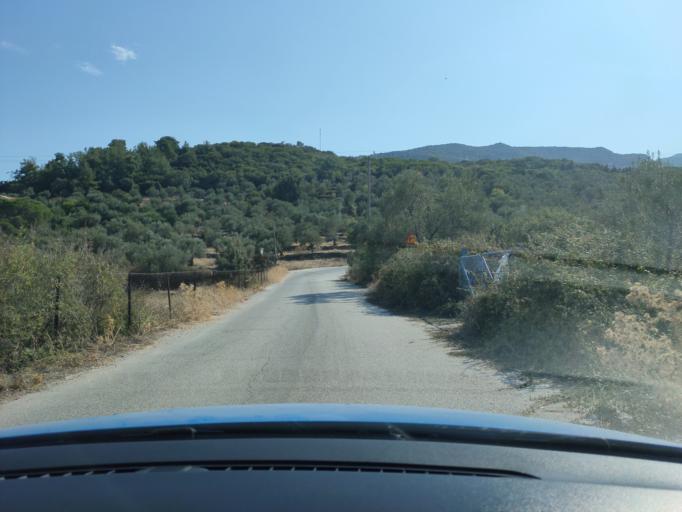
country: GR
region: North Aegean
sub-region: Nomos Lesvou
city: Mantamados
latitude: 39.3731
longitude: 26.3076
